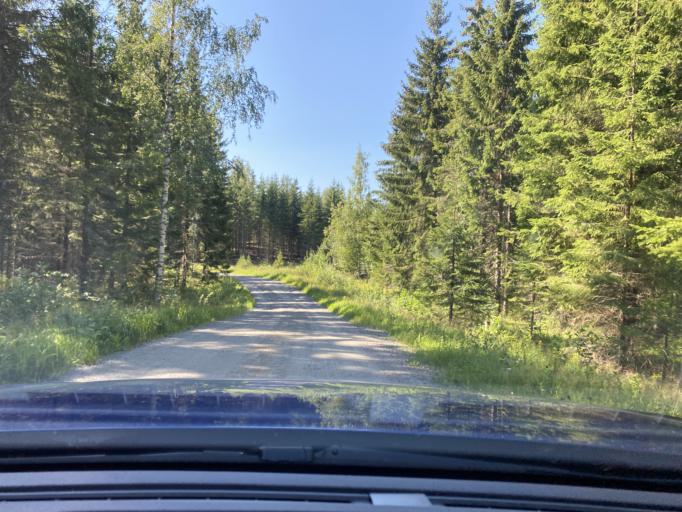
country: FI
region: Central Finland
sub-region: Jaemsae
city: Jaemsae
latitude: 61.8438
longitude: 25.3711
